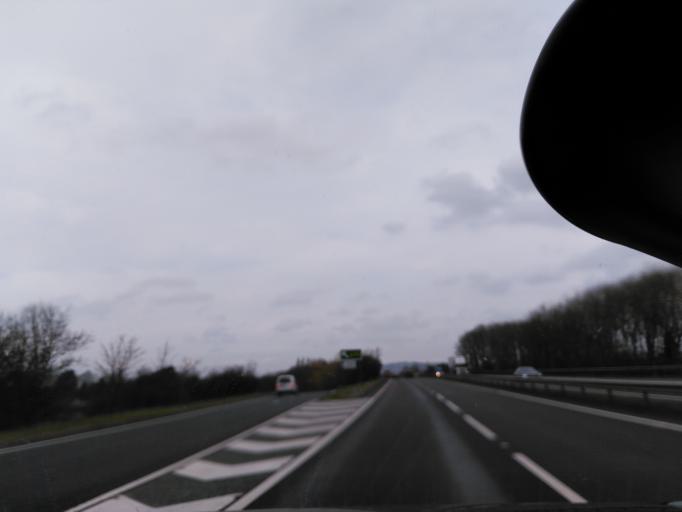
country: GB
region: England
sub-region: North Yorkshire
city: Thirsk
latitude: 54.2259
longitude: -1.3275
